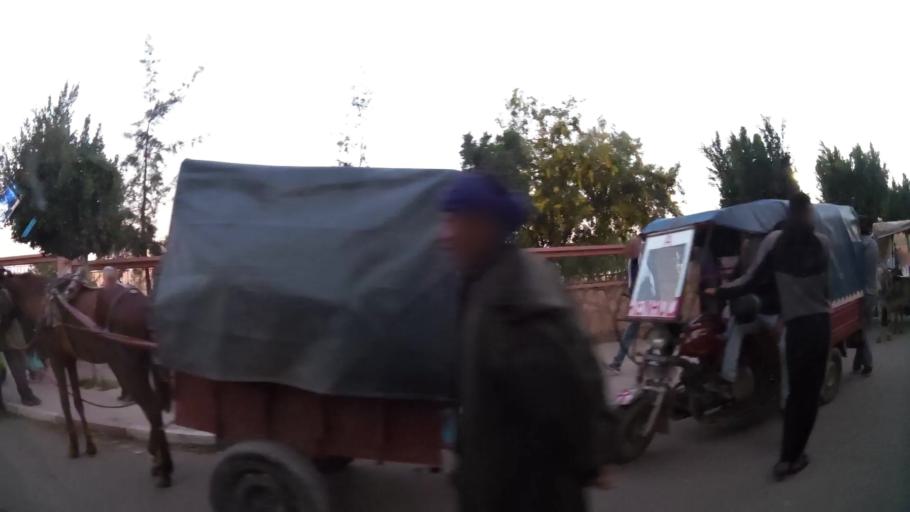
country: MA
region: Marrakech-Tensift-Al Haouz
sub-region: Kelaa-Des-Sraghna
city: Sidi Bou Othmane
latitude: 32.2281
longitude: -7.9458
